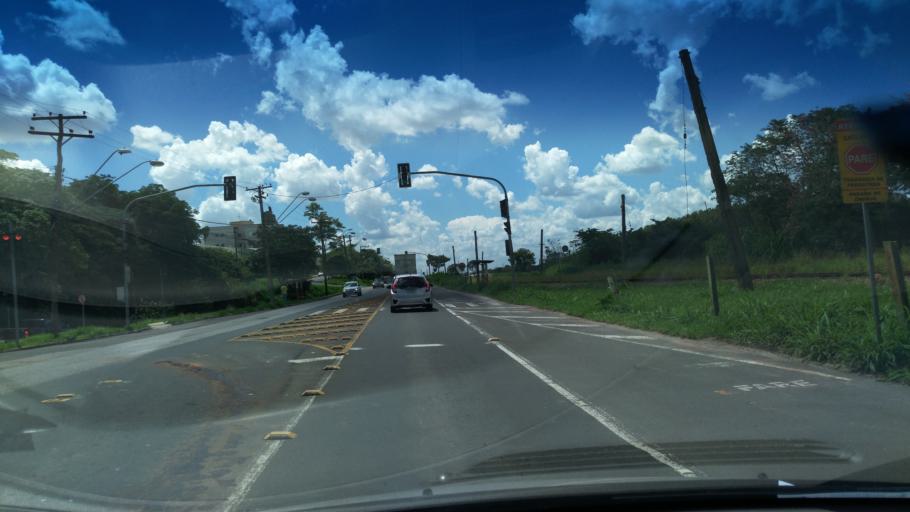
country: BR
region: Sao Paulo
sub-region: Valinhos
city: Valinhos
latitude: -23.0006
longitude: -46.9891
